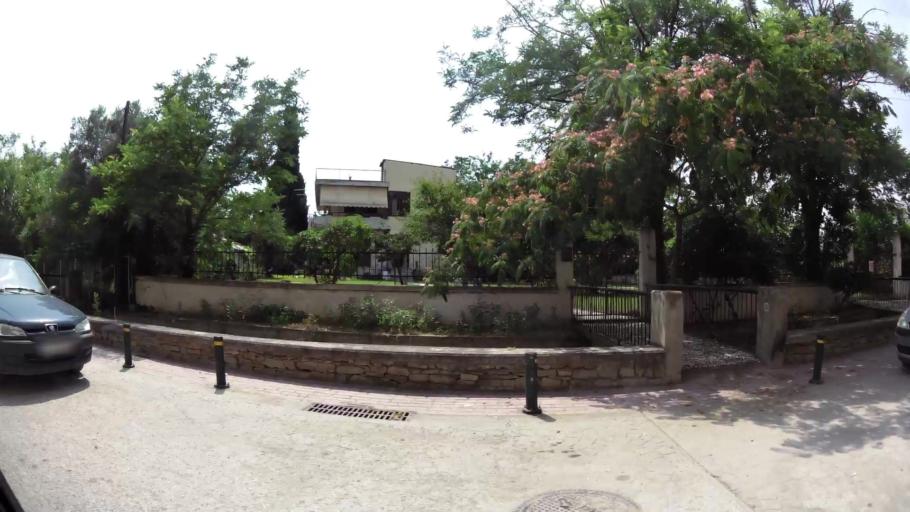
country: GR
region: Central Macedonia
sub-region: Nomos Thessalonikis
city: Diavata
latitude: 40.6898
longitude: 22.8538
